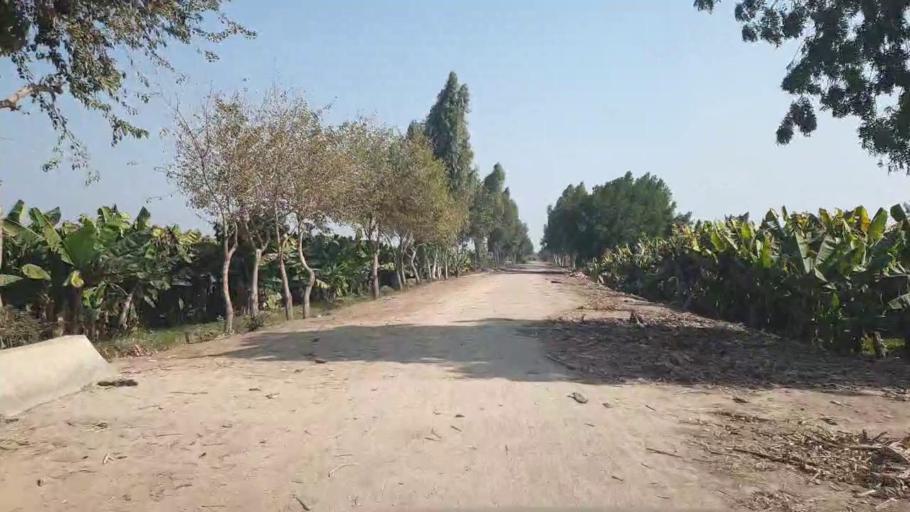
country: PK
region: Sindh
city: Tando Adam
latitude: 25.7985
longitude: 68.6263
